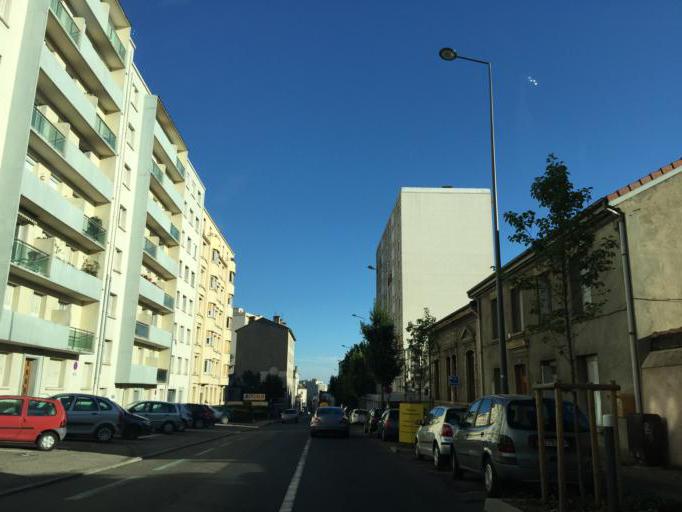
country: FR
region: Rhone-Alpes
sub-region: Departement de la Loire
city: Saint-Etienne
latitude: 45.4118
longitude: 4.3976
